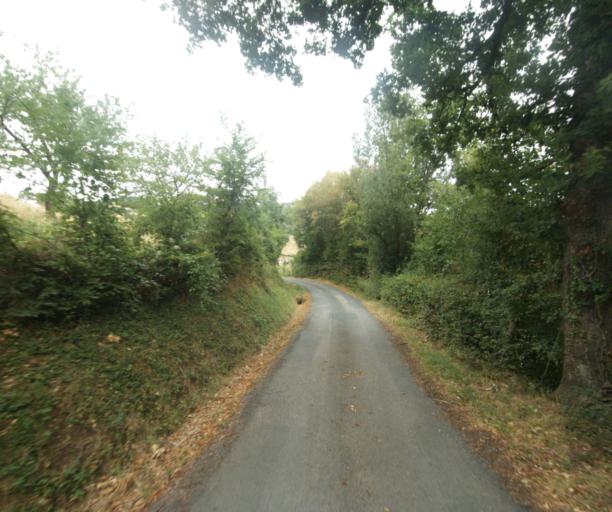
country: FR
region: Rhone-Alpes
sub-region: Departement du Rhone
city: Bessenay
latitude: 45.7888
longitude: 4.5179
